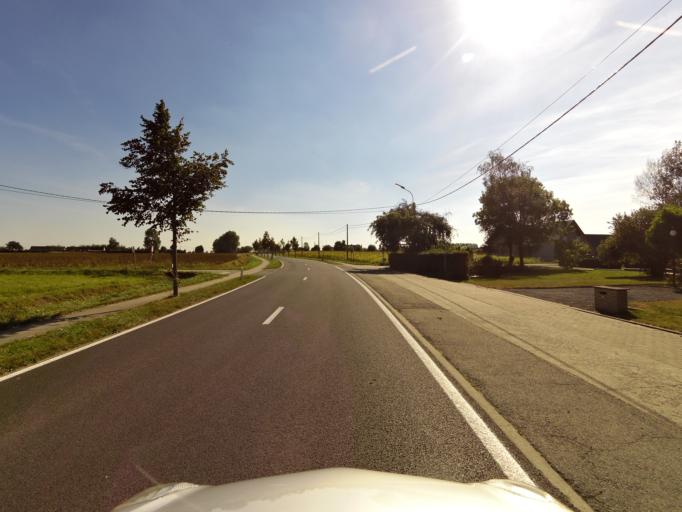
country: BE
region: Flanders
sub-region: Provincie West-Vlaanderen
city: Poperinge
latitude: 50.8957
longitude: 2.7396
